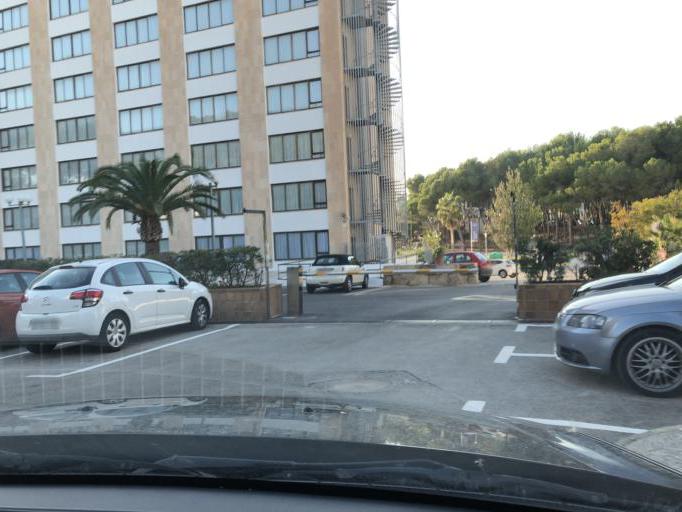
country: ES
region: Balearic Islands
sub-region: Illes Balears
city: Santa Ponsa
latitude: 39.5353
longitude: 2.4594
